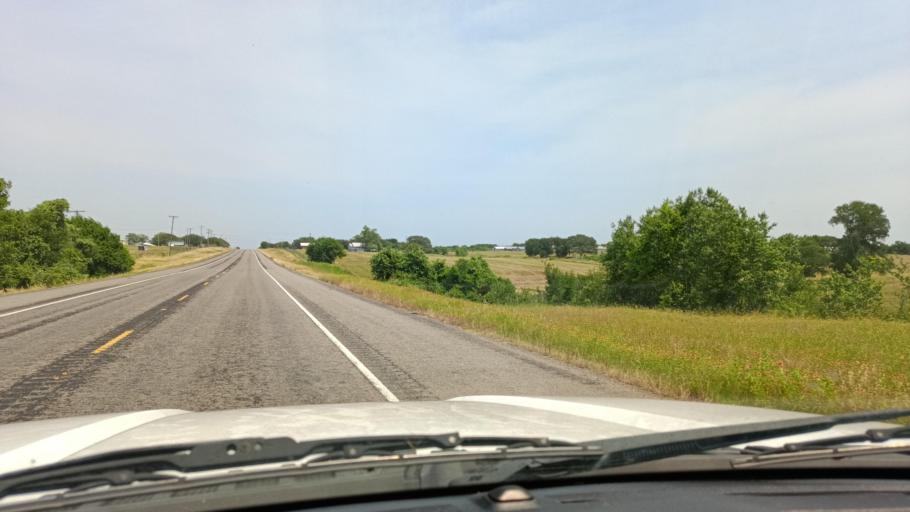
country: US
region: Texas
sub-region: Milam County
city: Cameron
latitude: 30.8539
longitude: -97.0955
